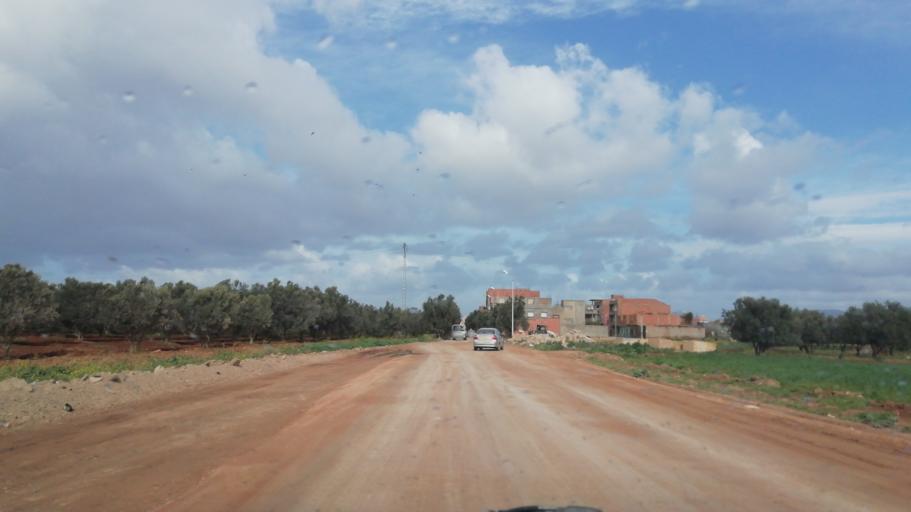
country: DZ
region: Oran
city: Sidi ech Chahmi
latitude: 35.6506
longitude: -0.5188
